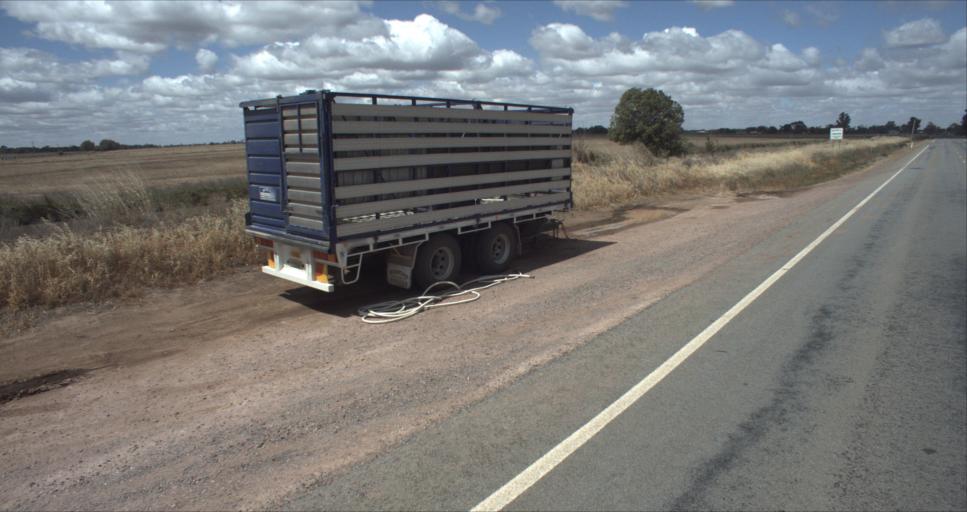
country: AU
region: New South Wales
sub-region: Murrumbidgee Shire
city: Darlington Point
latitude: -34.5110
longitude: 146.1863
